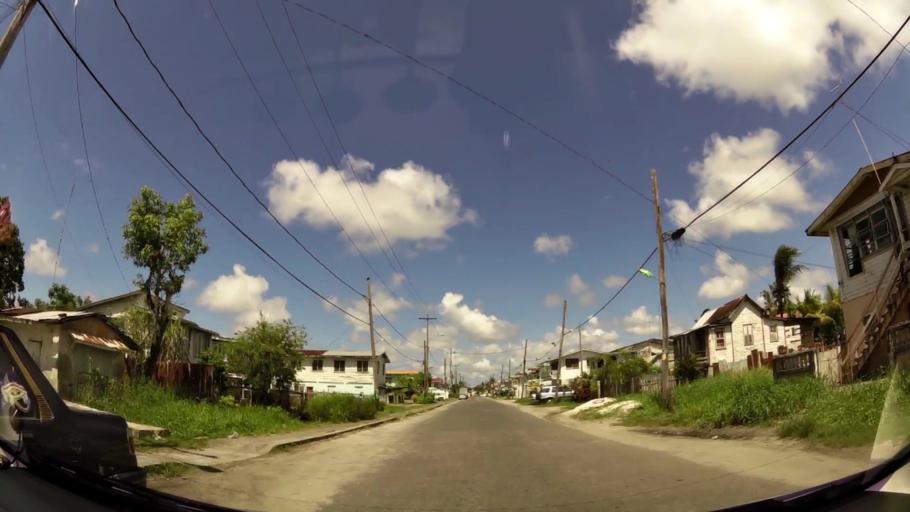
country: GY
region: Demerara-Mahaica
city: Georgetown
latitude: 6.8004
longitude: -58.1431
